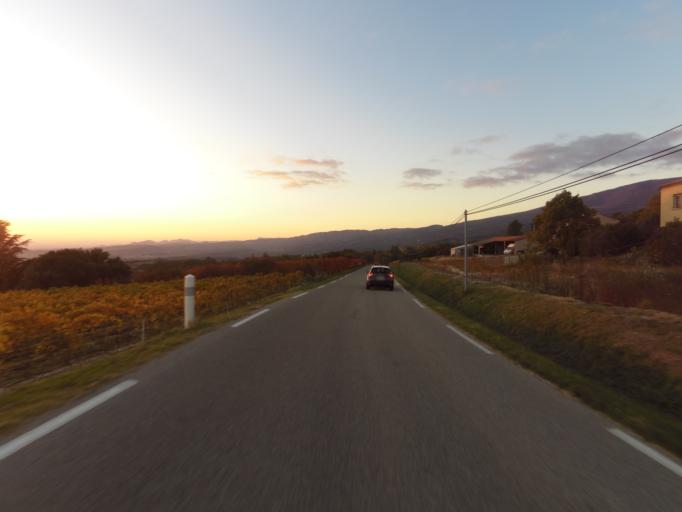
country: FR
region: Provence-Alpes-Cote d'Azur
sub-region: Departement du Vaucluse
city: Bedoin
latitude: 44.1179
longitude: 5.2338
